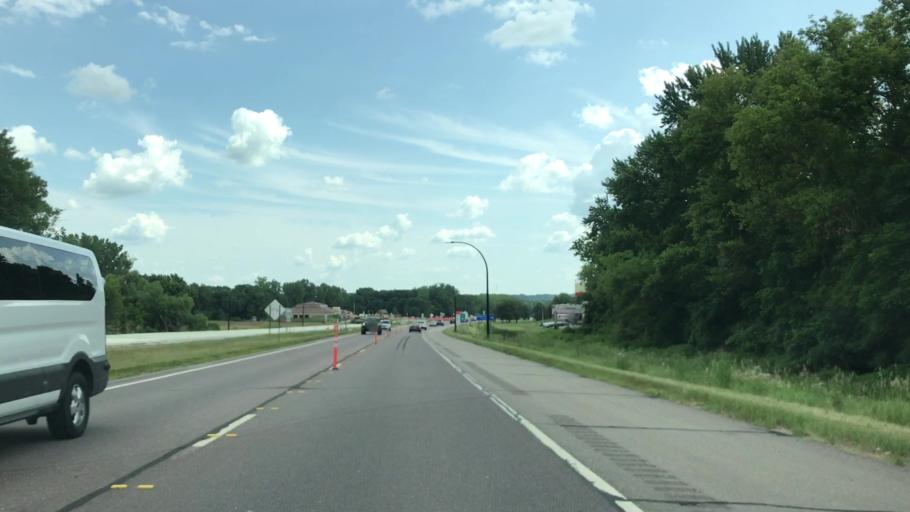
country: US
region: Minnesota
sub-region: Nicollet County
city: Saint Peter
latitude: 44.3527
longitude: -93.9537
